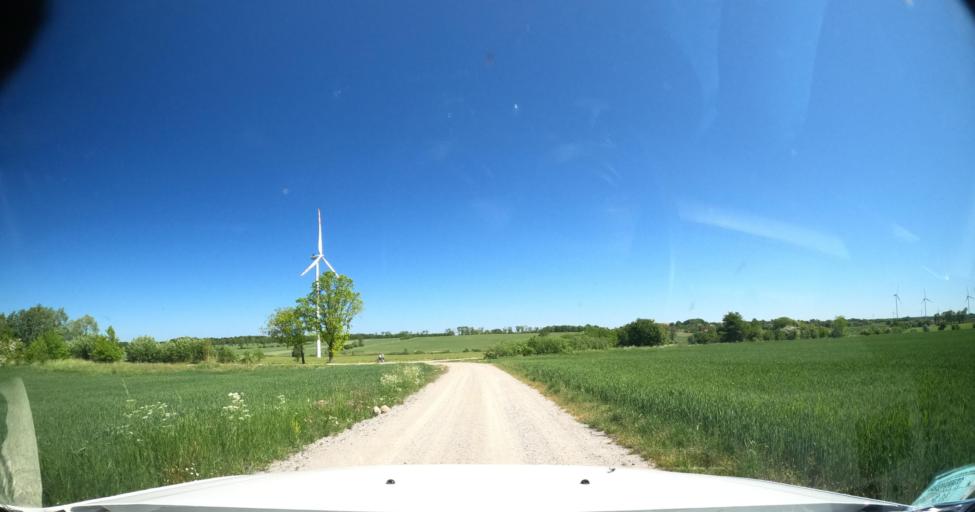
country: PL
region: Pomeranian Voivodeship
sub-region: Powiat slupski
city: Ustka
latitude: 54.5129
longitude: 16.7483
